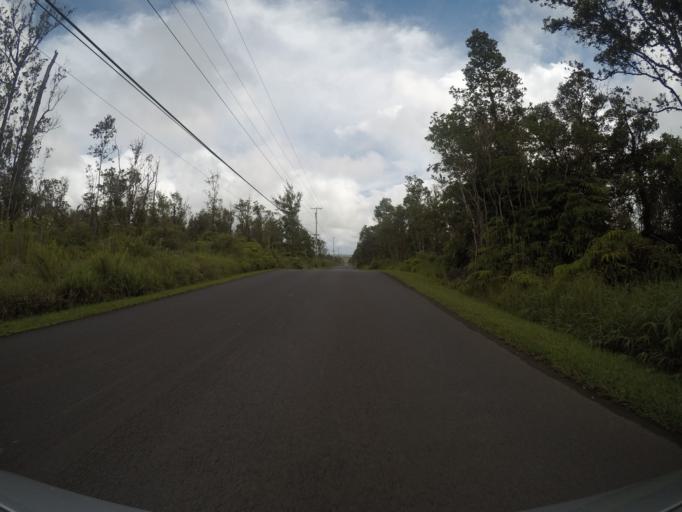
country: US
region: Hawaii
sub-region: Hawaii County
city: Fern Acres
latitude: 19.4708
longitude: -155.1375
